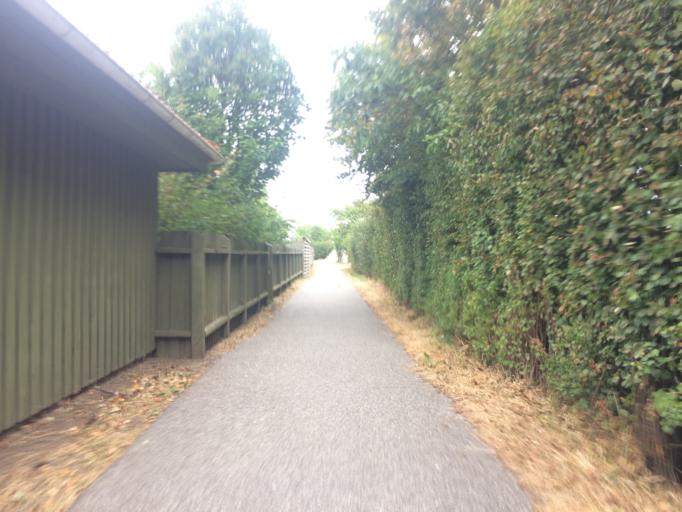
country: DK
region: Central Jutland
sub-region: Struer Kommune
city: Struer
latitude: 56.4876
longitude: 8.6100
